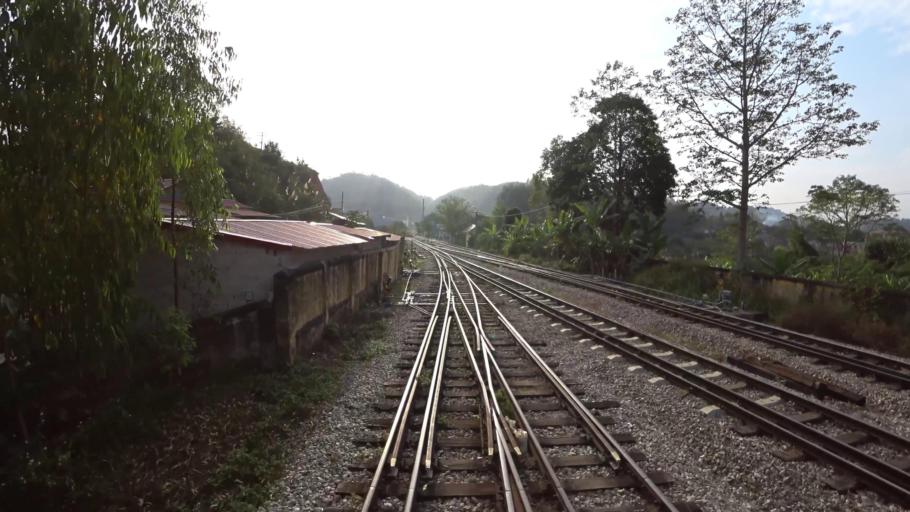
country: VN
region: Lang Son
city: Thi Tran Cao Loc
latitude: 21.9396
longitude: 106.6942
